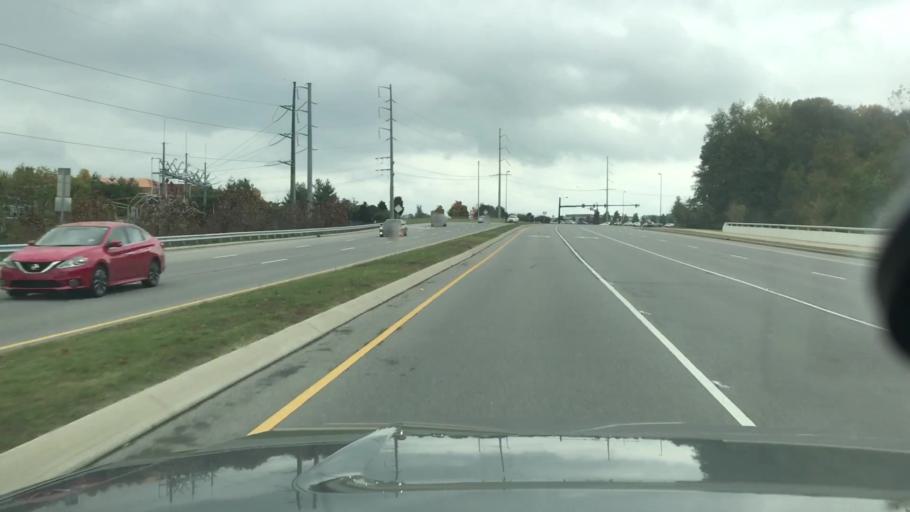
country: US
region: Tennessee
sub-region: Williamson County
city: Franklin
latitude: 35.9423
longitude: -86.8420
